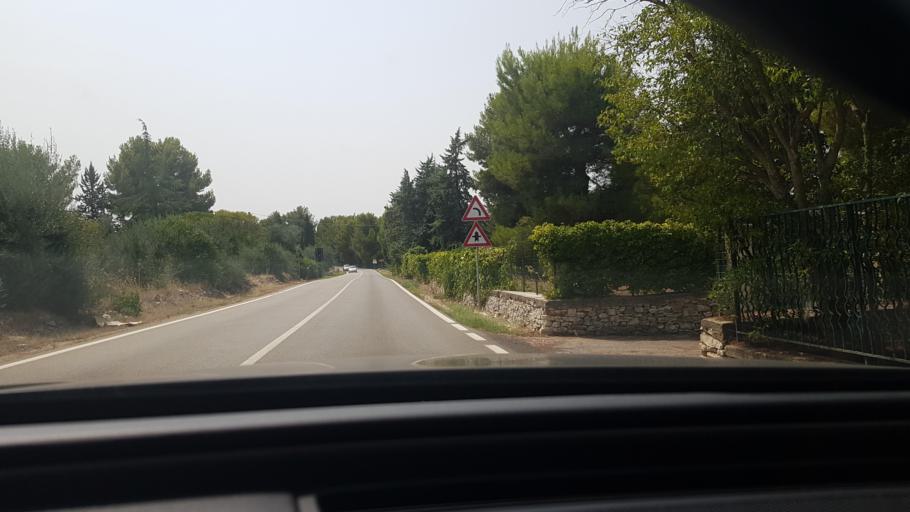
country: IT
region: Apulia
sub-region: Provincia di Barletta - Andria - Trani
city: Andria
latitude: 41.1288
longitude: 16.2889
